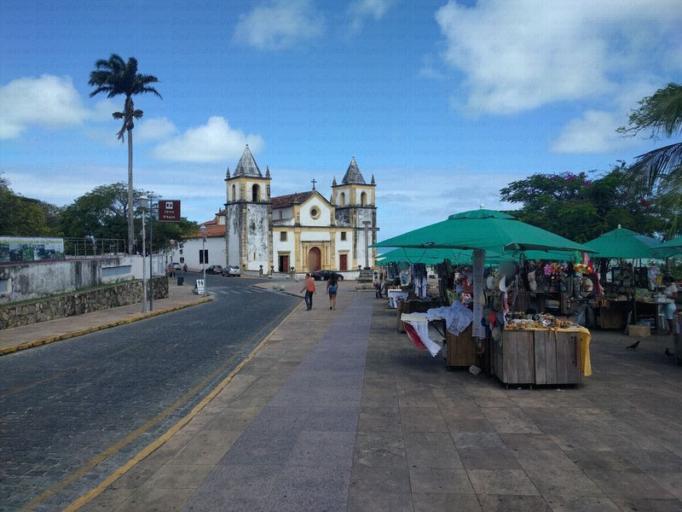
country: BR
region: Pernambuco
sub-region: Olinda
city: Olinda
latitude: -8.0136
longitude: -34.8501
